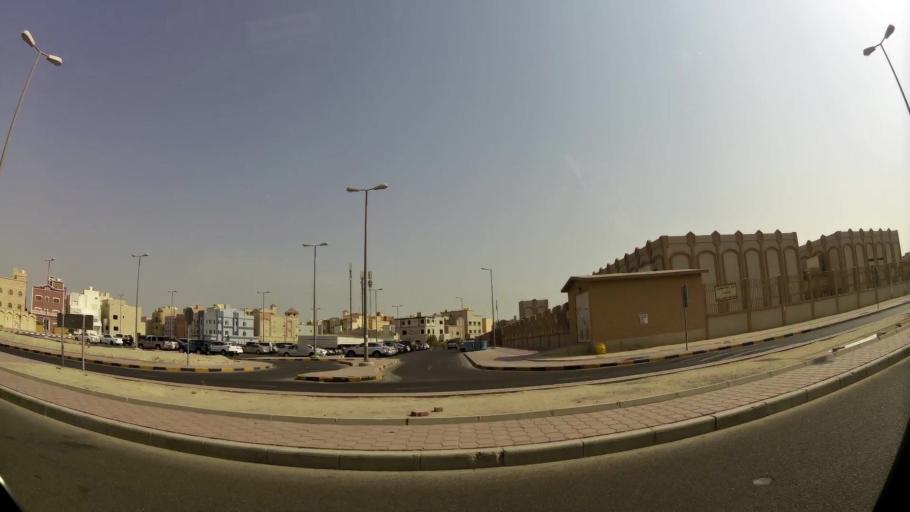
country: KW
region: Muhafazat al Jahra'
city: Al Jahra'
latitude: 29.3388
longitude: 47.7691
